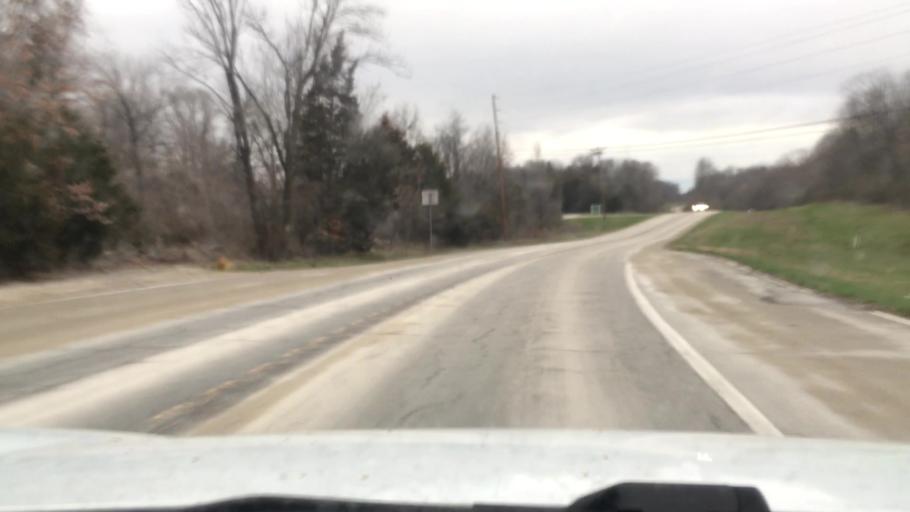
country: US
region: Missouri
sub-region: Saint Charles County
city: Weldon Spring
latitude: 38.6822
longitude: -90.7343
